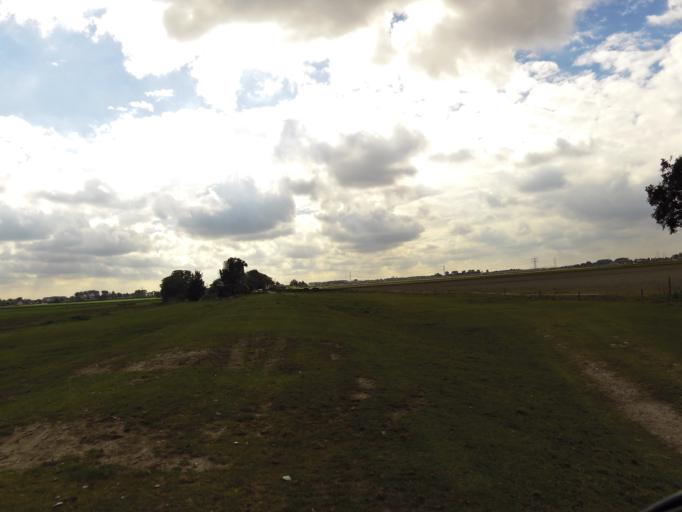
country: NL
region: South Holland
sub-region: Gemeente Rijnwoude
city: Benthuizen
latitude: 52.0525
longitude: 4.5641
